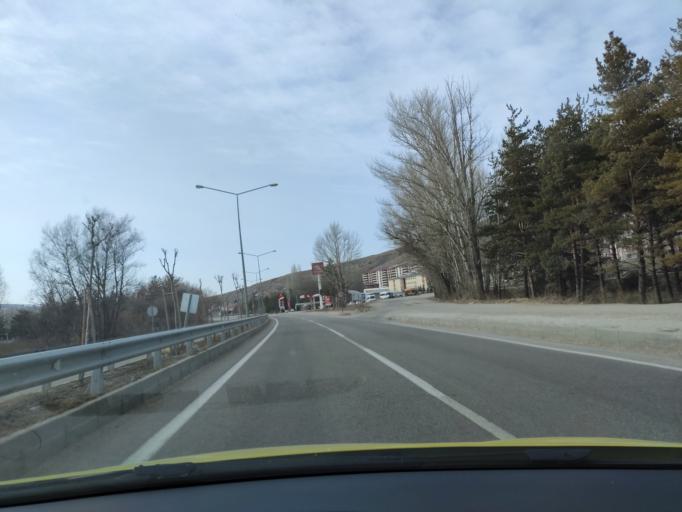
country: TR
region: Bayburt
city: Bayburt
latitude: 40.2381
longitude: 40.2515
